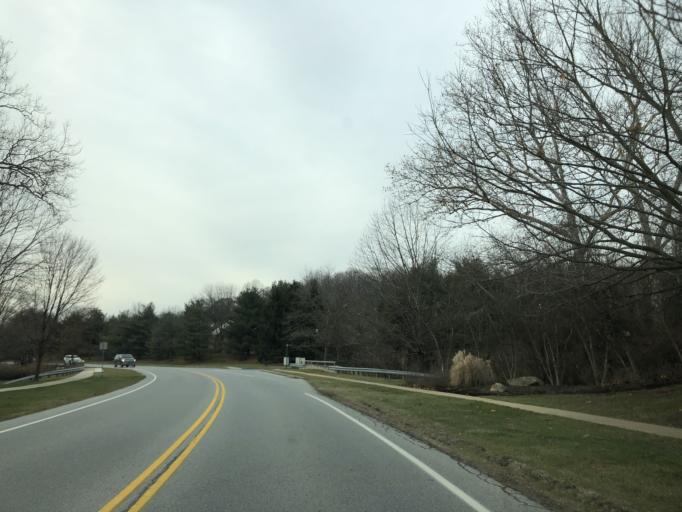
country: US
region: Pennsylvania
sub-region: Chester County
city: Exton
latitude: 40.0334
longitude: -75.6347
